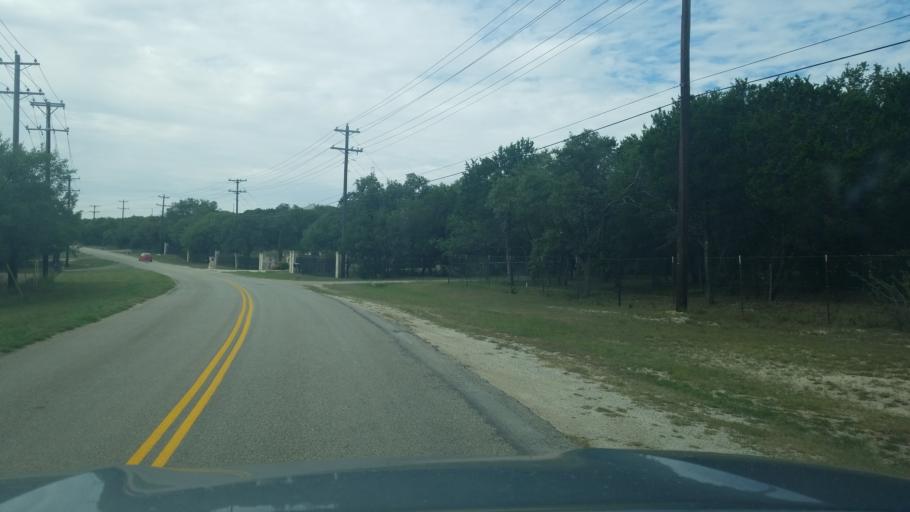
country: US
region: Texas
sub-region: Comal County
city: Bulverde
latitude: 29.7823
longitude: -98.4143
